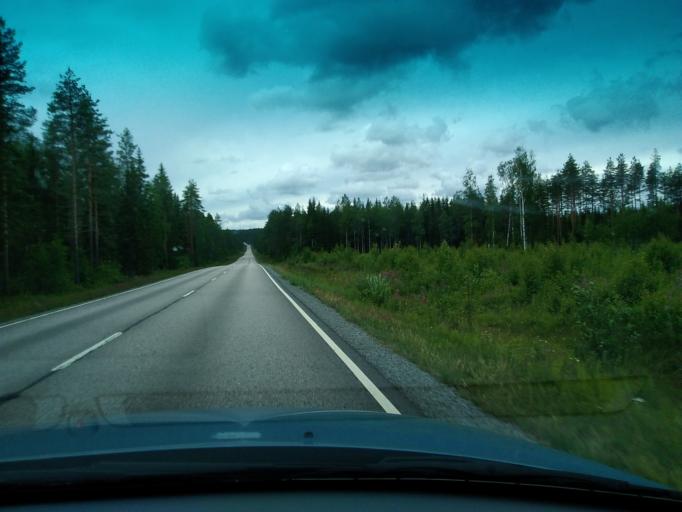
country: FI
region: Central Finland
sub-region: Saarijaervi-Viitasaari
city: Pylkoenmaeki
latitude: 62.5977
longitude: 24.6242
